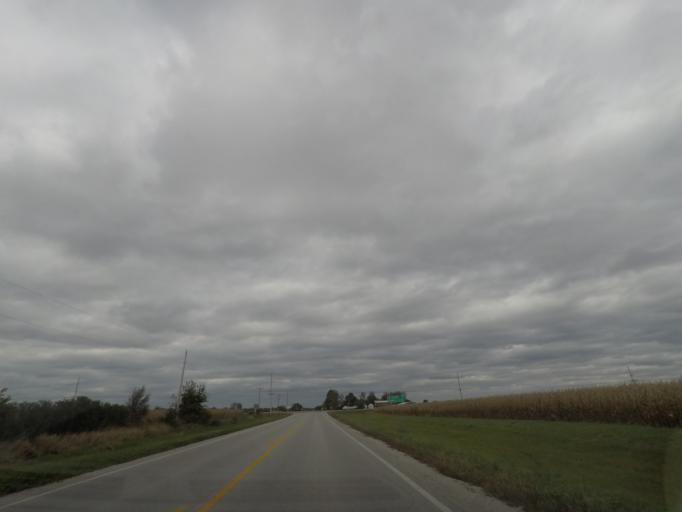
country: US
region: Iowa
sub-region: Story County
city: Huxley
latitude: 41.8764
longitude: -93.5314
